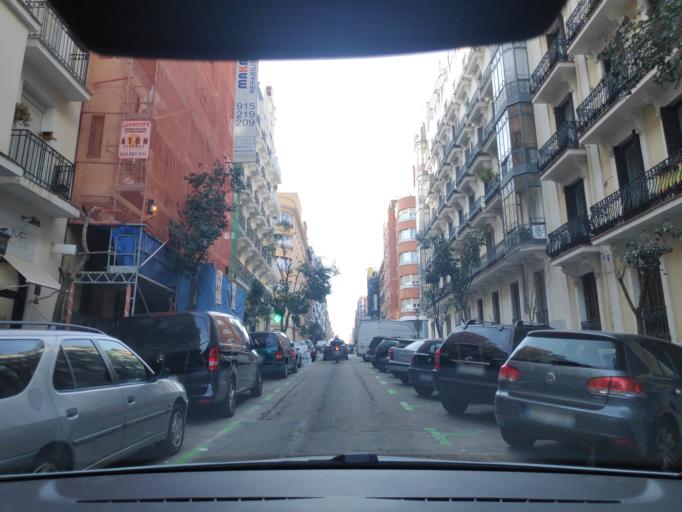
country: ES
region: Madrid
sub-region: Provincia de Madrid
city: Salamanca
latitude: 40.4368
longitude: -3.6843
